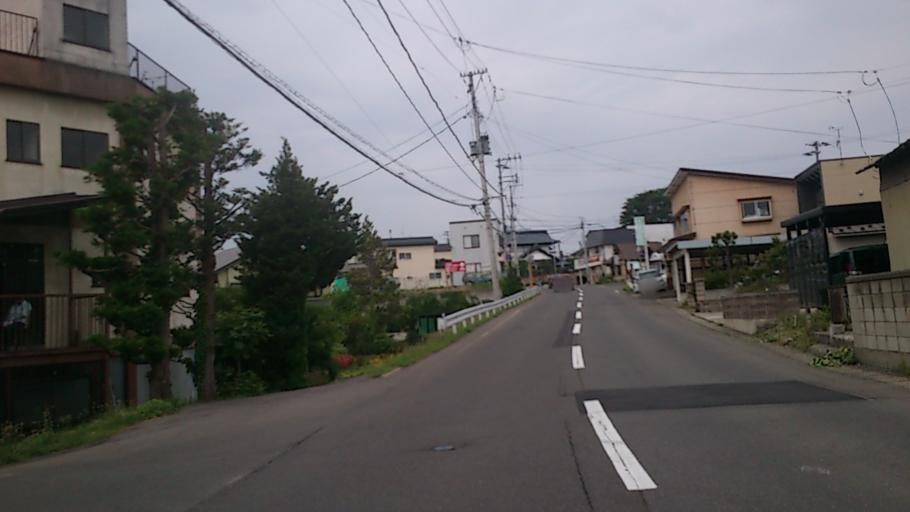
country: JP
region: Aomori
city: Hirosaki
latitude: 40.5945
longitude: 140.4539
